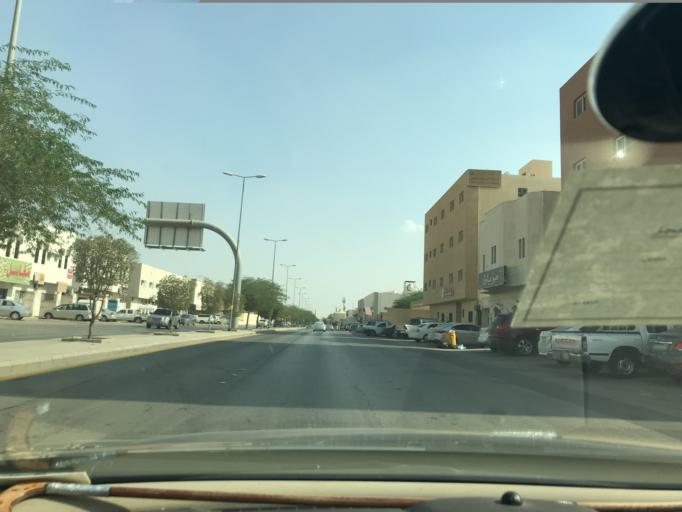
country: SA
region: Ar Riyad
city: Riyadh
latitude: 24.7473
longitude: 46.7623
